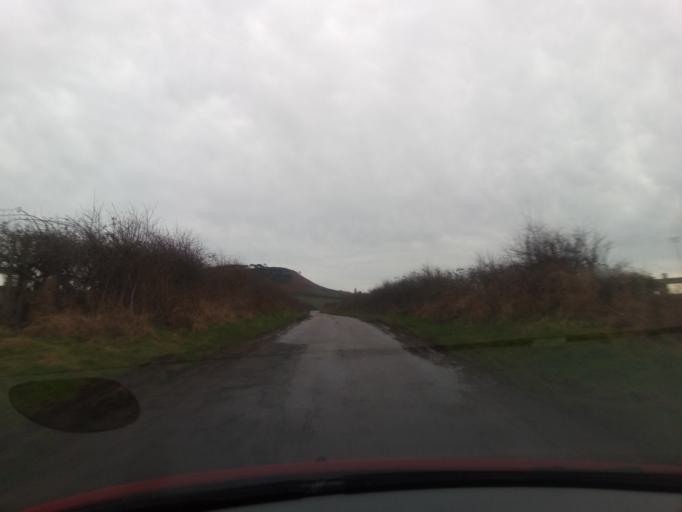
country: GB
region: England
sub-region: Northumberland
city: Whittingham
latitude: 55.4937
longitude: -1.9061
